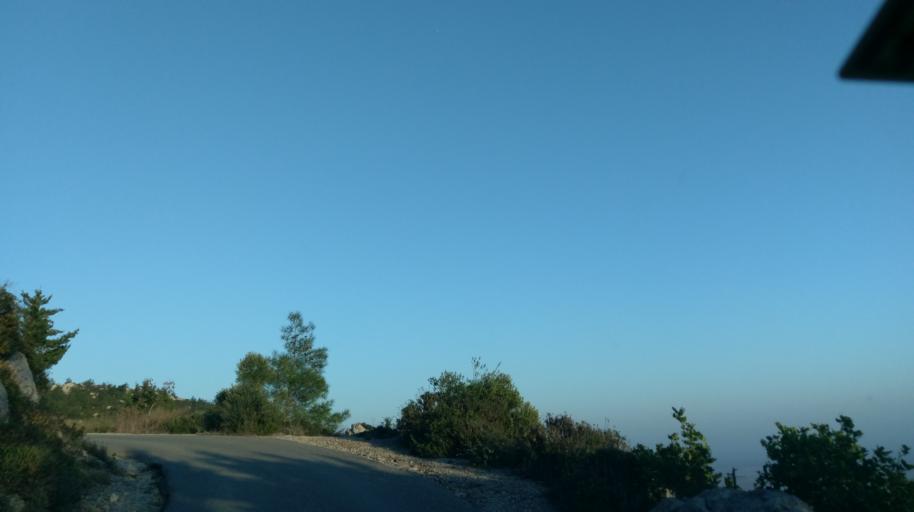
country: CY
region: Ammochostos
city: Trikomo
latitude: 35.4023
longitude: 33.9180
